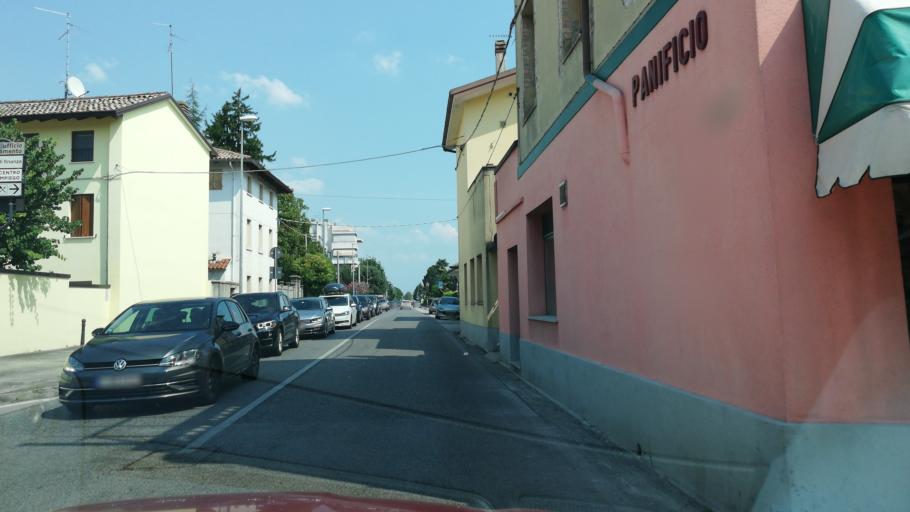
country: IT
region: Friuli Venezia Giulia
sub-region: Provincia di Udine
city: Latisana
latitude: 45.7794
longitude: 12.9975
